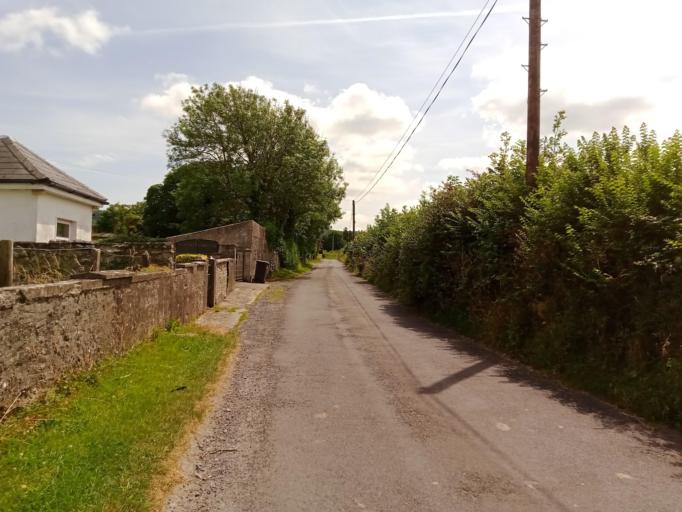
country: IE
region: Leinster
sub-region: Laois
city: Rathdowney
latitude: 52.8138
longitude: -7.4709
